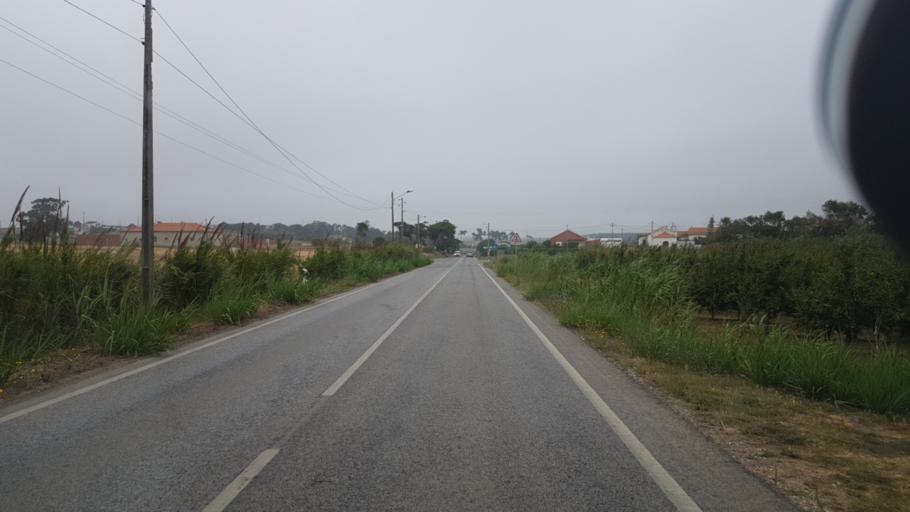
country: PT
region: Lisbon
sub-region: Torres Vedras
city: Silveira
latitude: 39.0915
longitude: -9.3559
